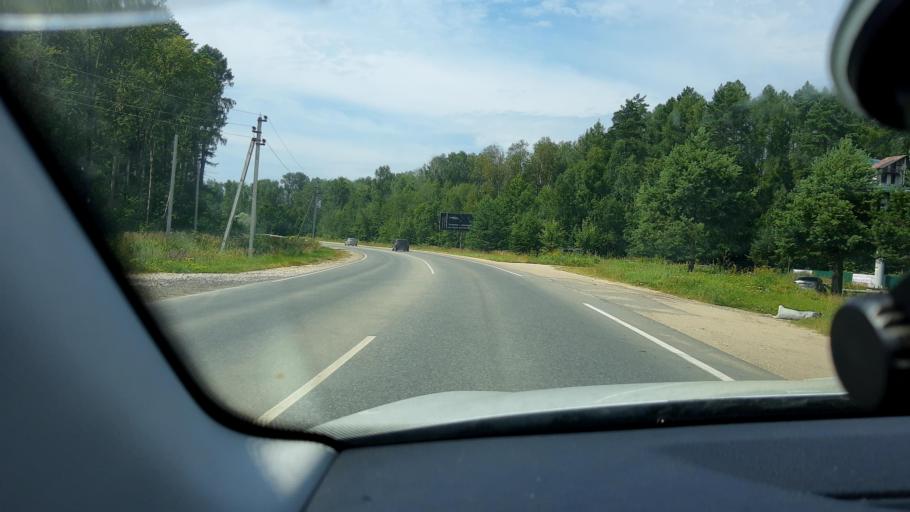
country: RU
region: Tula
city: Zaokskiy
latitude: 54.7477
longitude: 37.4036
